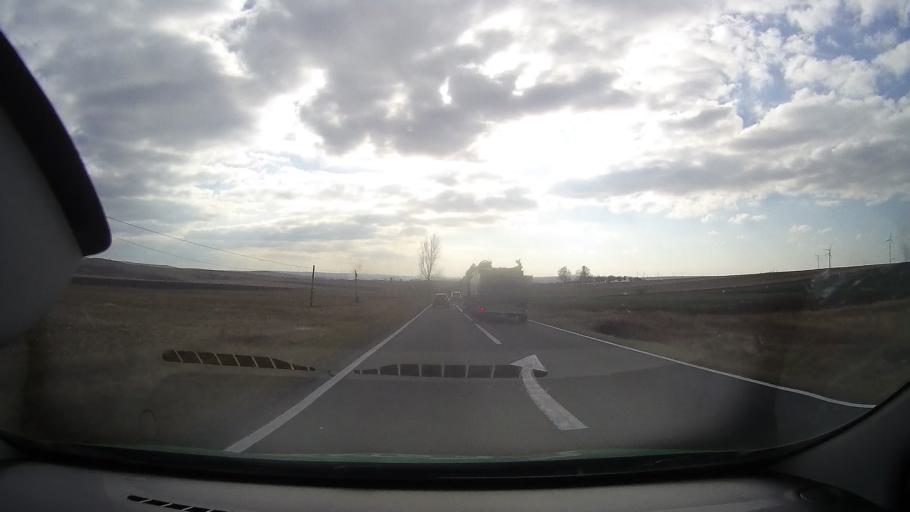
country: RO
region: Tulcea
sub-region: Comuna Topolog
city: Topolog
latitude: 44.8912
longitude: 28.3940
